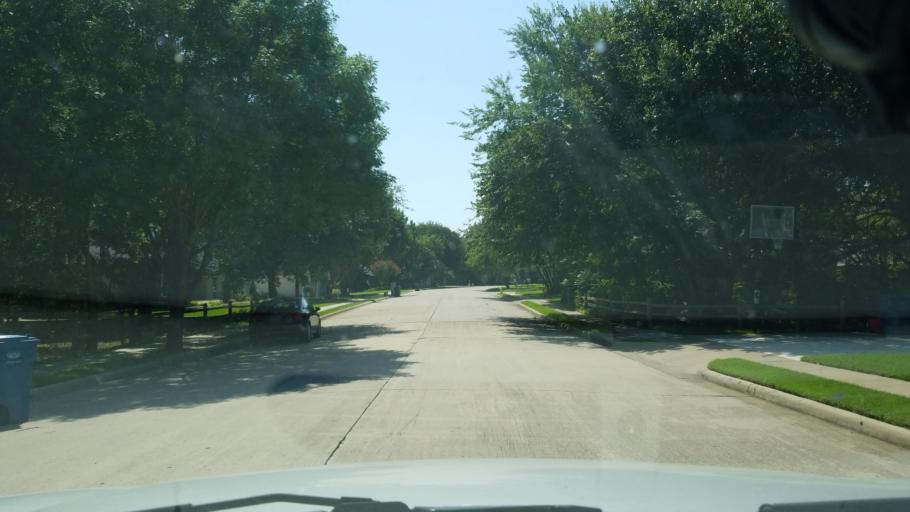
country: US
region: Texas
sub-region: Dallas County
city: Coppell
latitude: 32.9542
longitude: -96.9864
